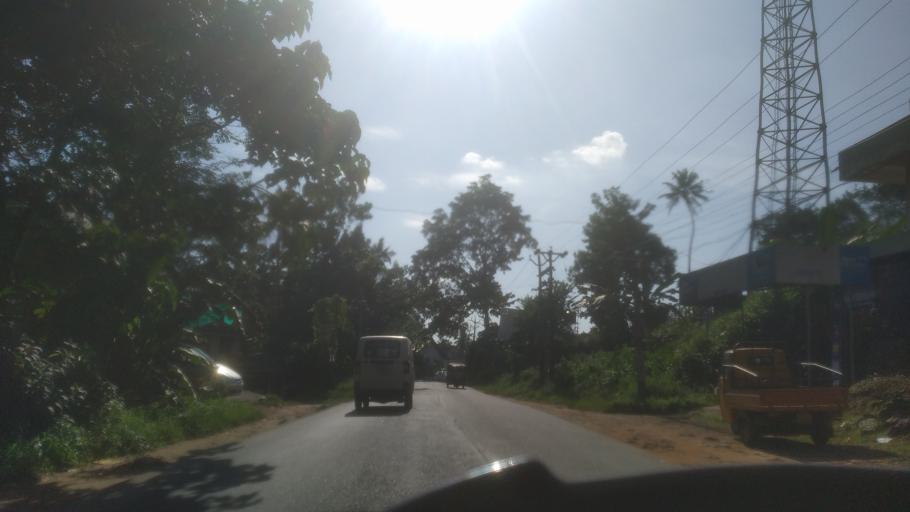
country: IN
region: Kerala
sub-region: Ernakulam
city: Muvattupuzha
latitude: 9.9800
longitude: 76.5528
